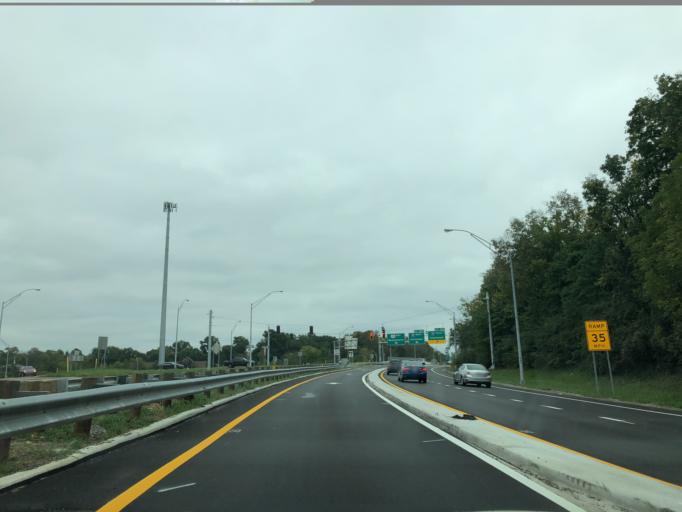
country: US
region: Ohio
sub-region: Hamilton County
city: Blue Ash
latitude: 39.2262
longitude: -84.3701
